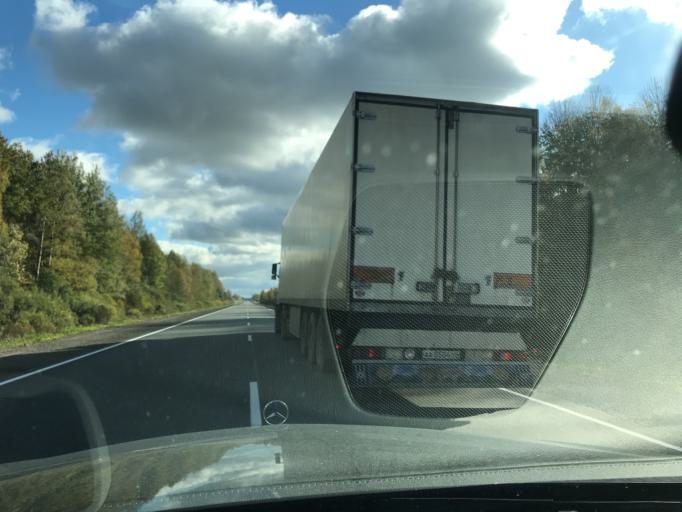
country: RU
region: Pskov
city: Pushkinskiye Gory
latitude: 57.0668
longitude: 28.5699
